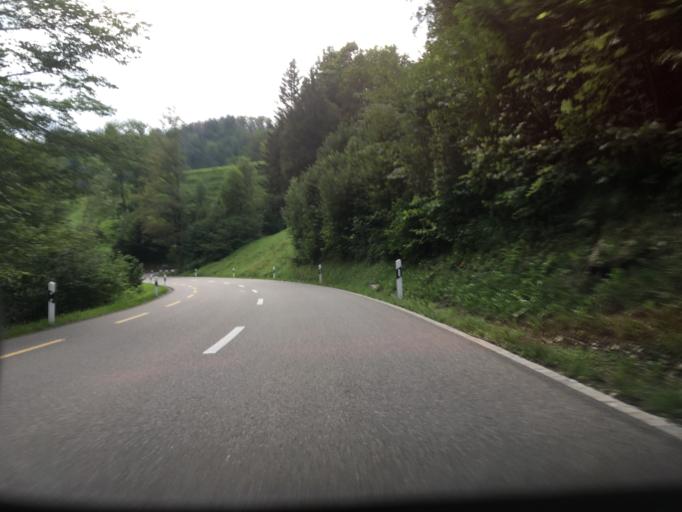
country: CH
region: Thurgau
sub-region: Muenchwilen District
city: Fischingen
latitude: 47.3497
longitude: 8.9477
